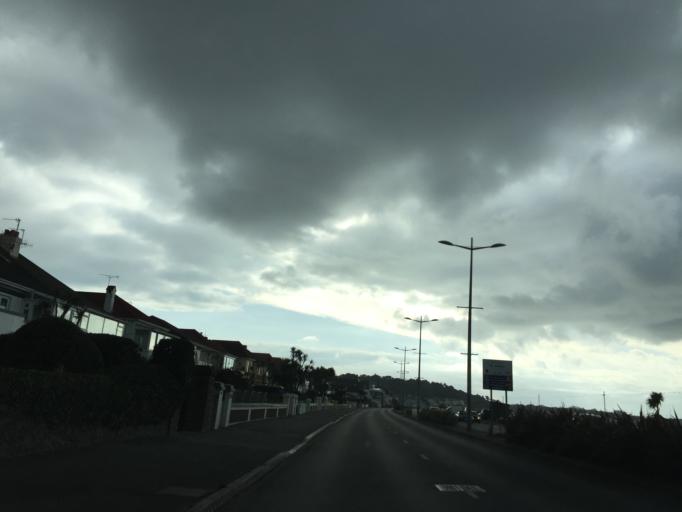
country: JE
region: St Helier
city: Saint Helier
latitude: 49.1966
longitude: -2.1370
